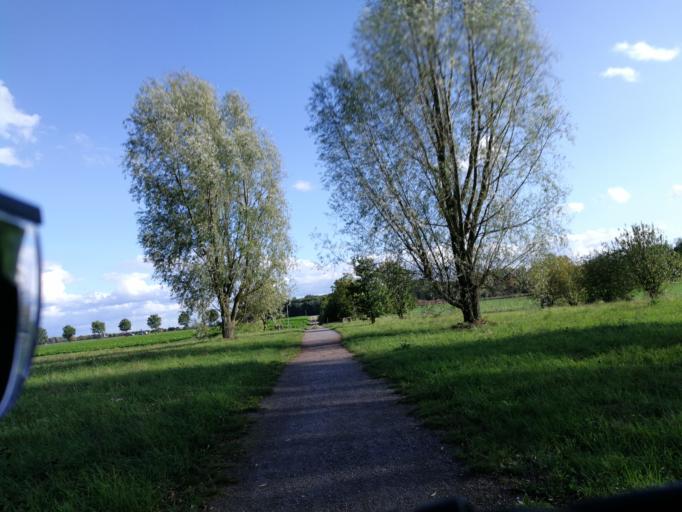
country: DE
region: North Rhine-Westphalia
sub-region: Regierungsbezirk Dusseldorf
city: Neuss
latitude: 51.1323
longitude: 6.7417
